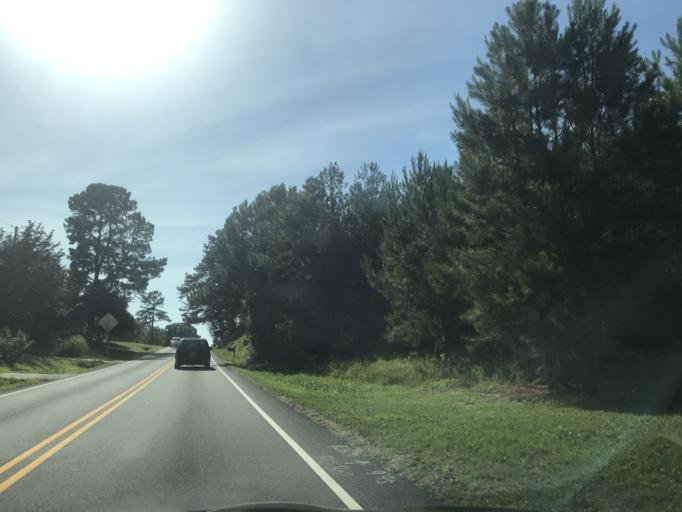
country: US
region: North Carolina
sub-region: Wake County
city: Garner
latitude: 35.6622
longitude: -78.5501
